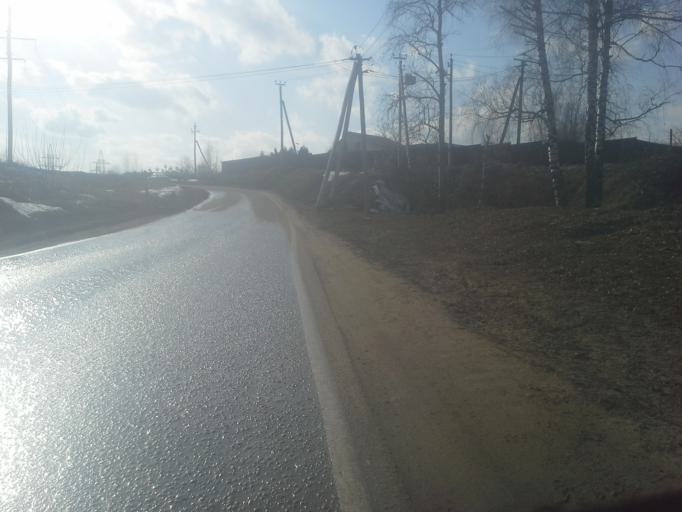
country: RU
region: Moskovskaya
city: Dubrovitsy
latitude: 55.4641
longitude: 37.5255
